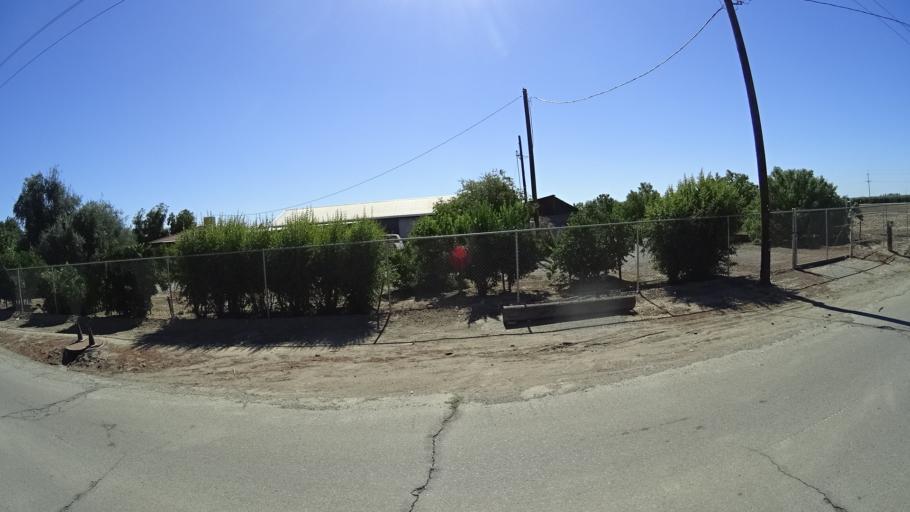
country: US
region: California
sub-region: Fresno County
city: West Park
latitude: 36.7016
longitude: -119.8089
